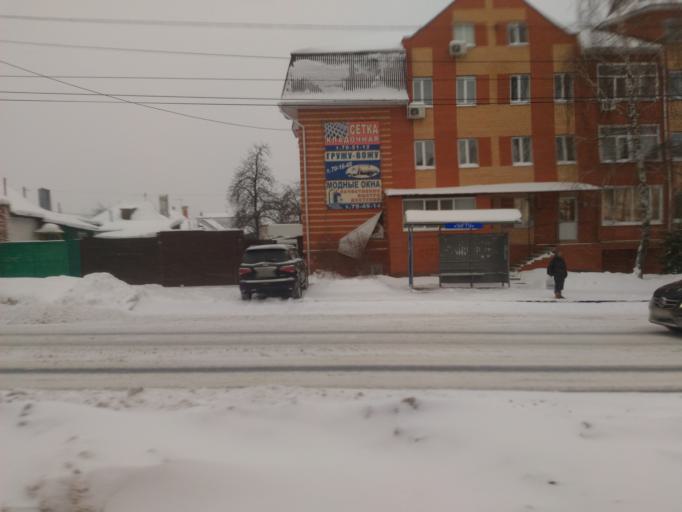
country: RU
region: Ulyanovsk
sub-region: Ulyanovskiy Rayon
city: Ulyanovsk
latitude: 54.3500
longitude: 48.3827
